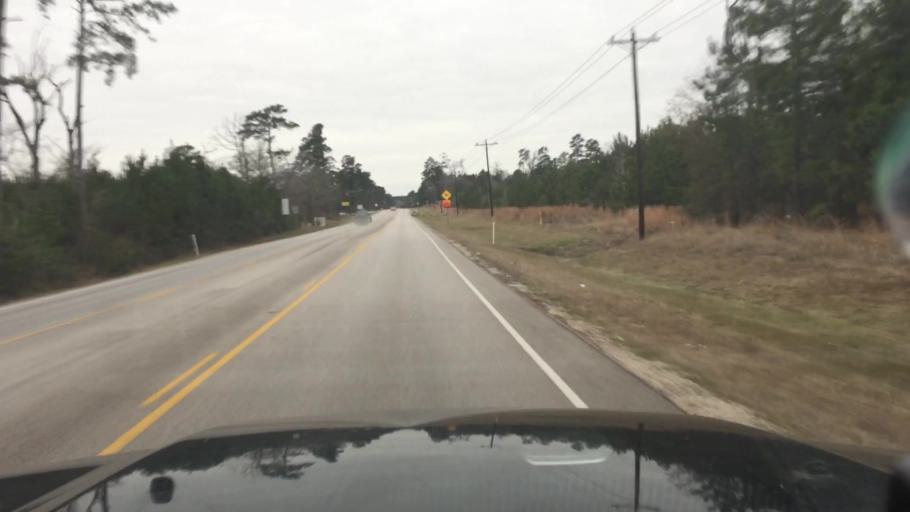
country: US
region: Texas
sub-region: Montgomery County
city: Magnolia
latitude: 30.1896
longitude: -95.8083
